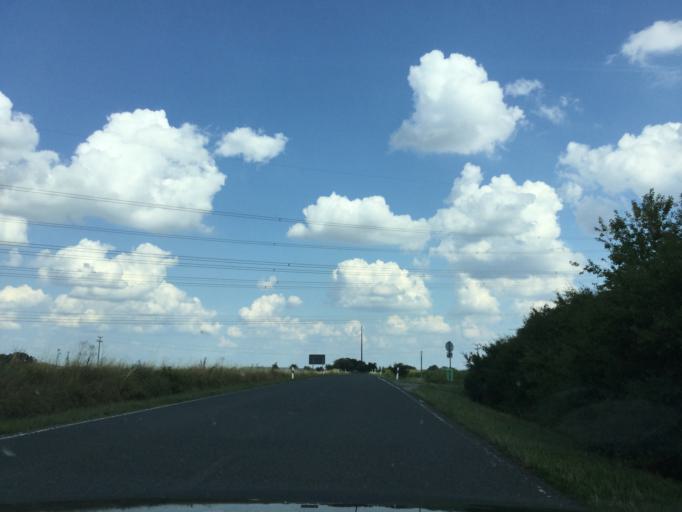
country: DE
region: Bavaria
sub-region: Regierungsbezirk Mittelfranken
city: Adelsdorf
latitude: 49.4804
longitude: 10.6915
